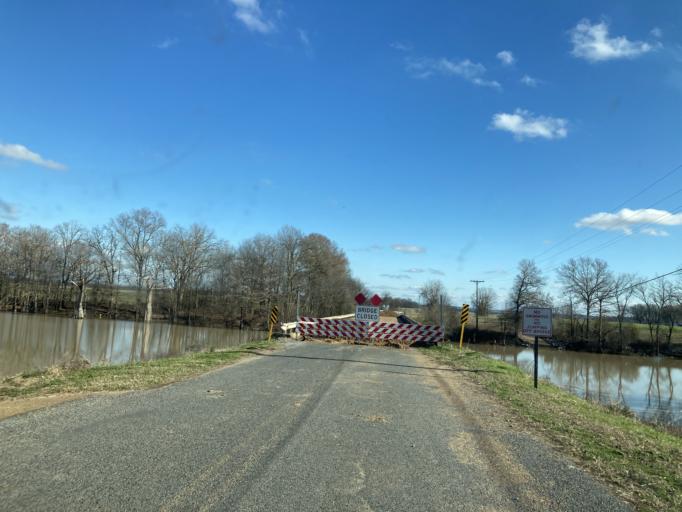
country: US
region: Mississippi
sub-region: Yazoo County
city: Yazoo City
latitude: 32.9256
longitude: -90.4685
